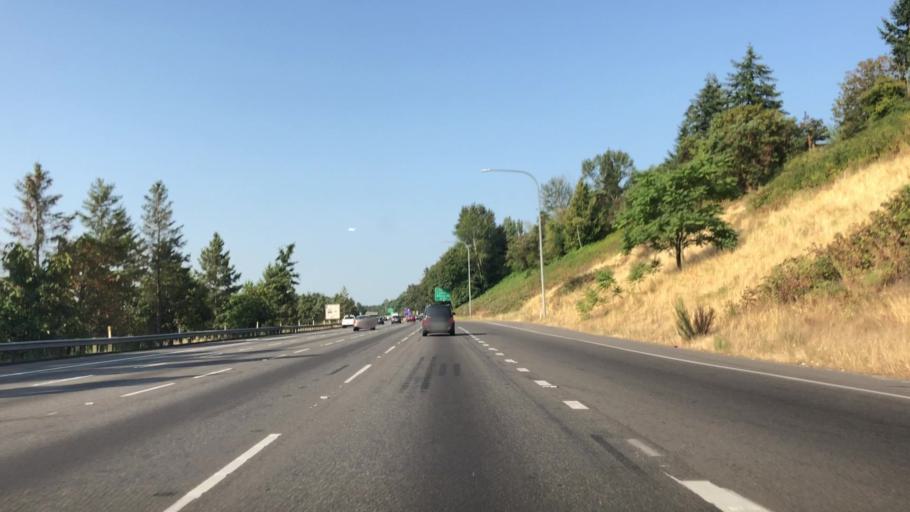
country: US
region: Washington
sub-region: King County
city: SeaTac
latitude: 47.4293
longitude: -122.2749
